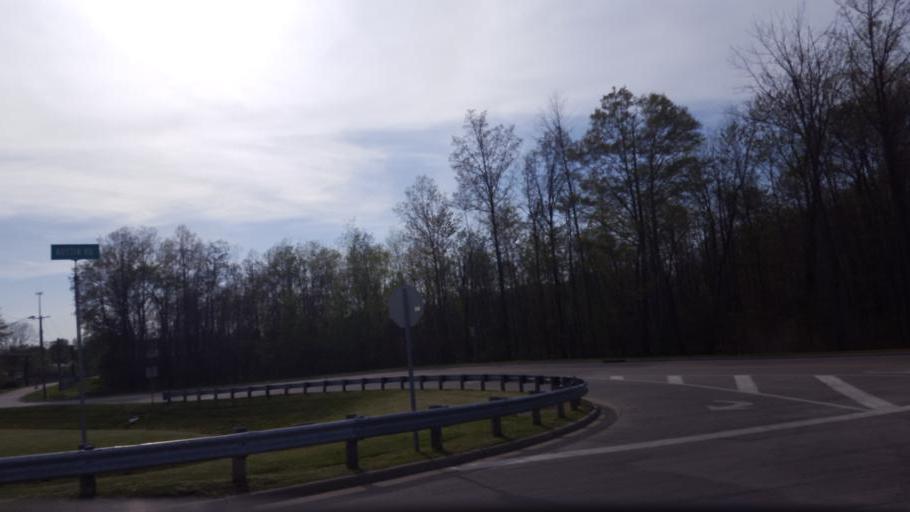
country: US
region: Ohio
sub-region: Ashtabula County
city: Geneva
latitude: 41.8129
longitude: -80.9370
